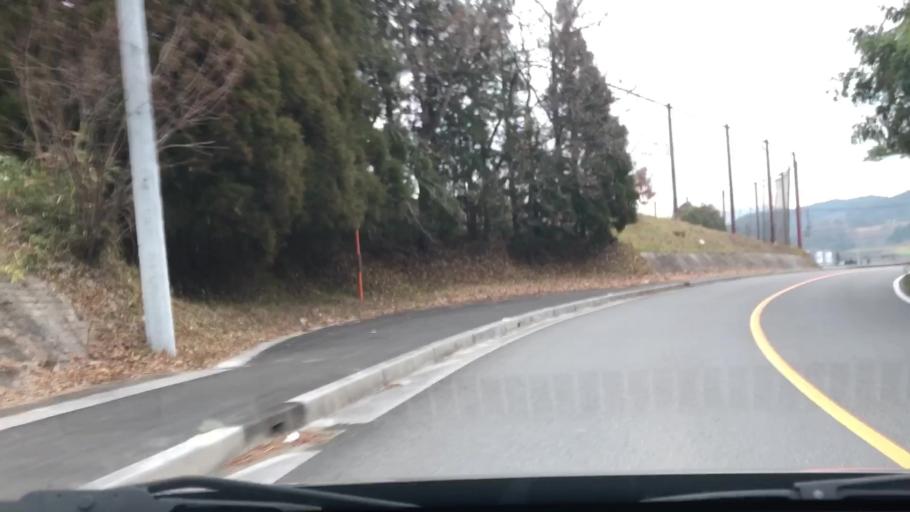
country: JP
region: Oita
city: Usuki
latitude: 33.0048
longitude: 131.6282
